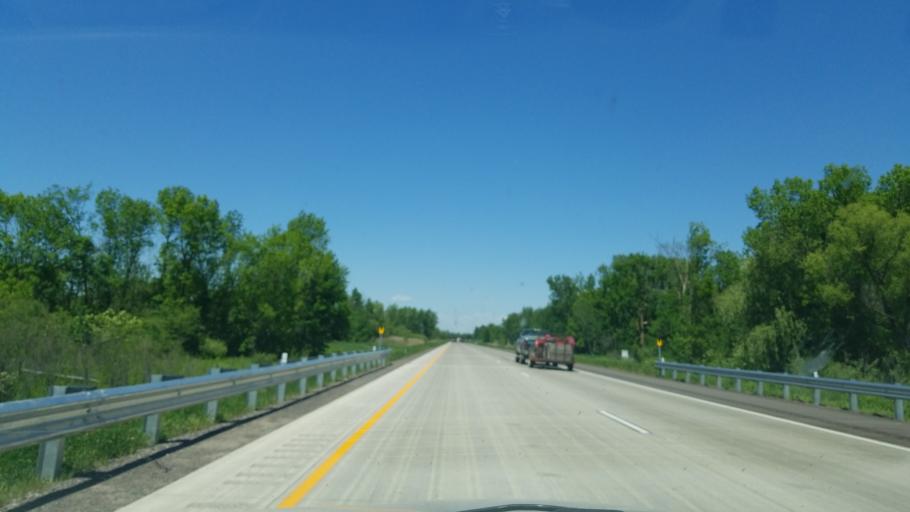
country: US
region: Minnesota
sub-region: Pine County
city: Hinckley
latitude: 45.9254
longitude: -92.9666
